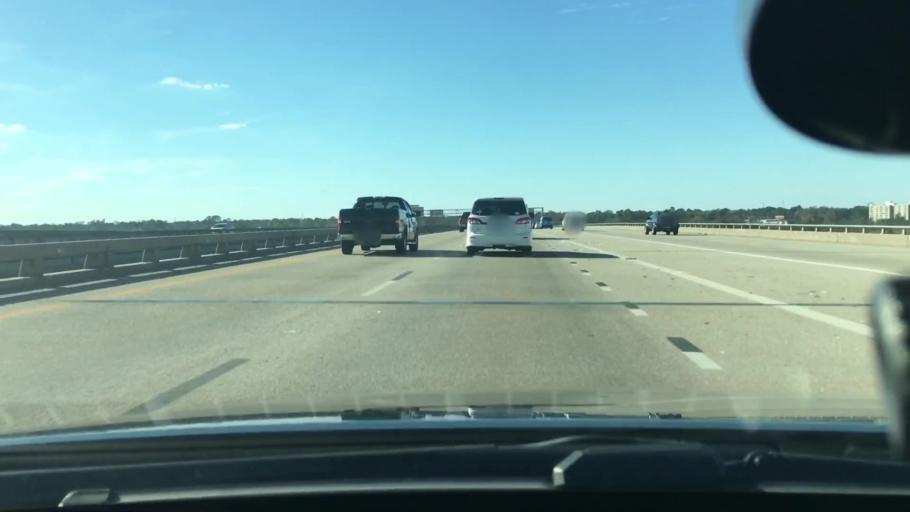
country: US
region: North Carolina
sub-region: Craven County
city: James City
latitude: 35.0955
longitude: -77.0435
